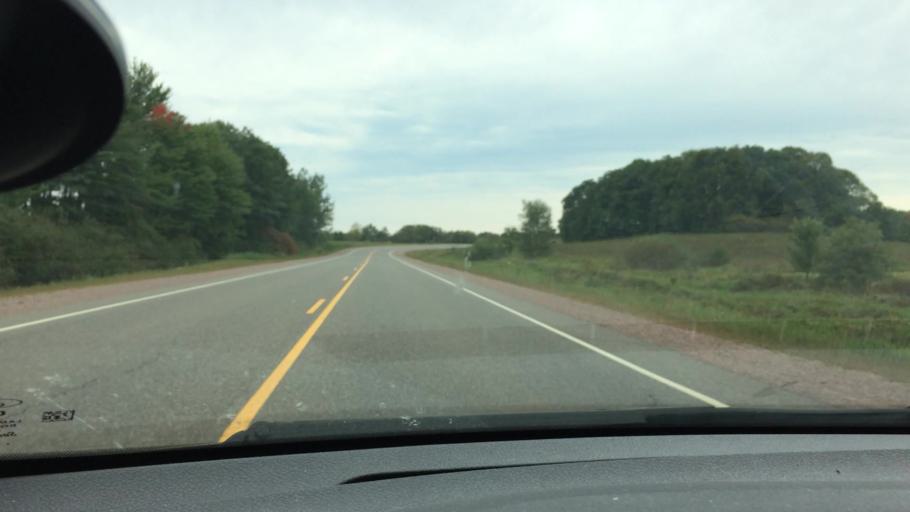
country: US
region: Wisconsin
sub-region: Clark County
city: Neillsville
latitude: 44.5532
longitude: -90.6340
